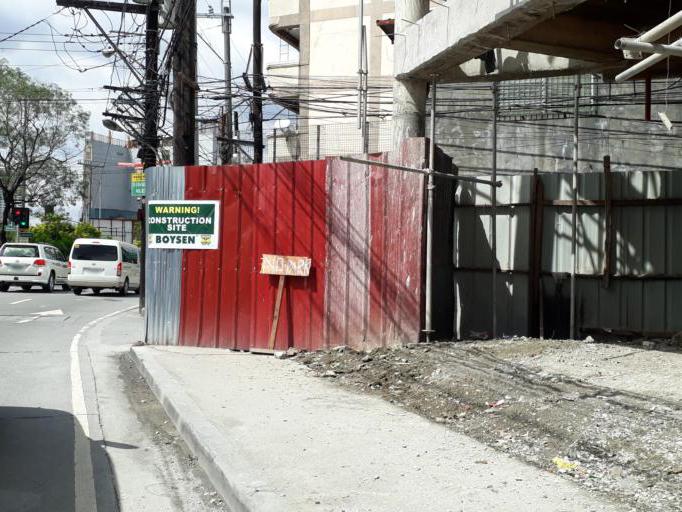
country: PH
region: Metro Manila
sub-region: City of Manila
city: Manila
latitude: 14.6113
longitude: 120.9863
